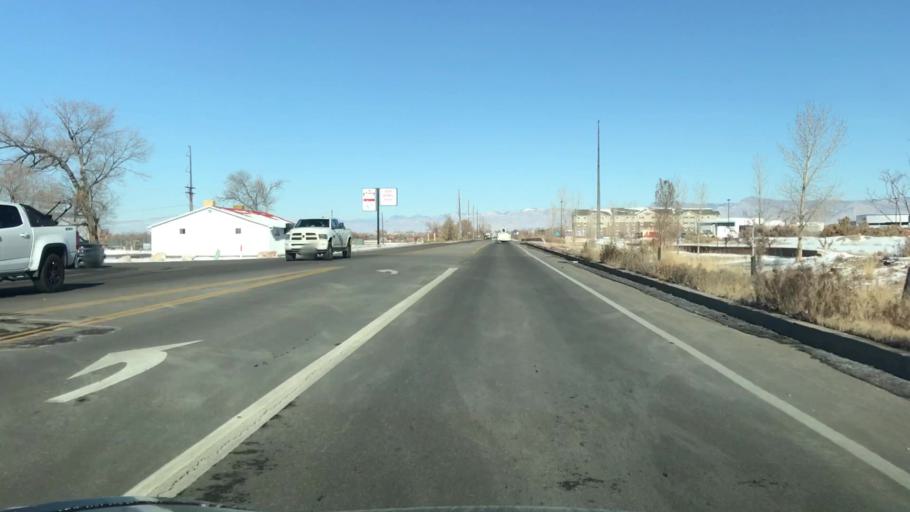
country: US
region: Colorado
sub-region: Mesa County
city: Redlands
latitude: 39.0969
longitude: -108.6081
